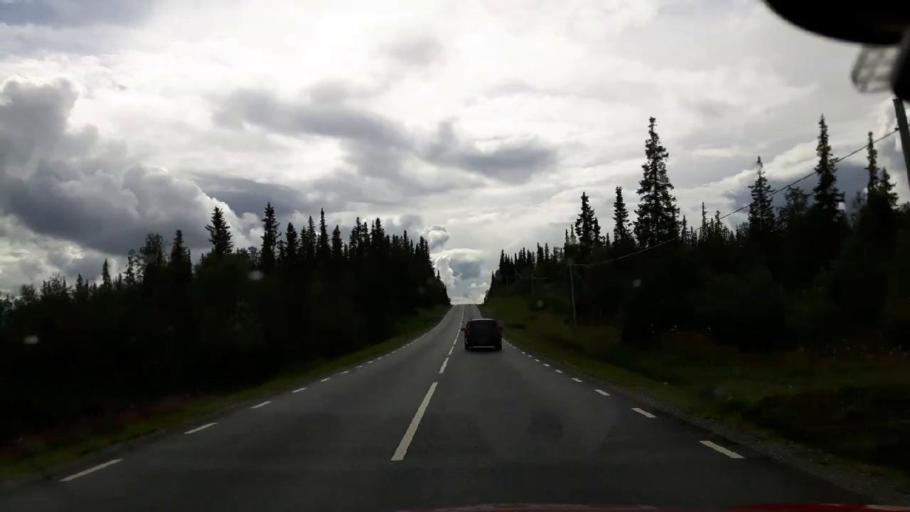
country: NO
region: Nord-Trondelag
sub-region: Royrvik
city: Royrvik
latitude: 64.8378
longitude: 14.1267
